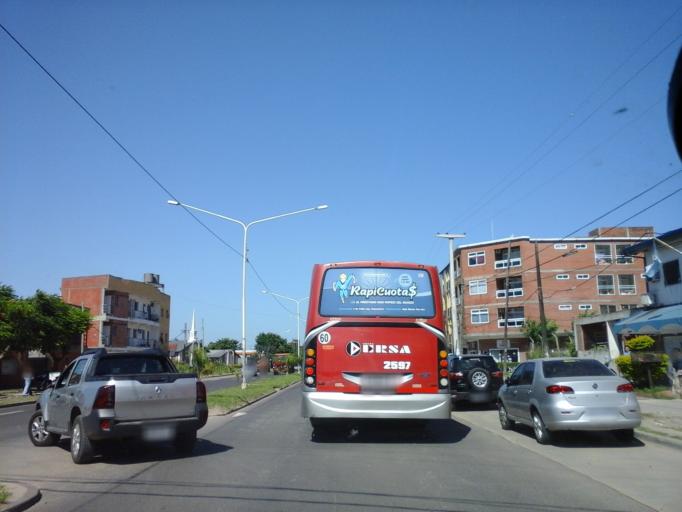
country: AR
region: Corrientes
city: Corrientes
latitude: -27.4663
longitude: -58.7883
